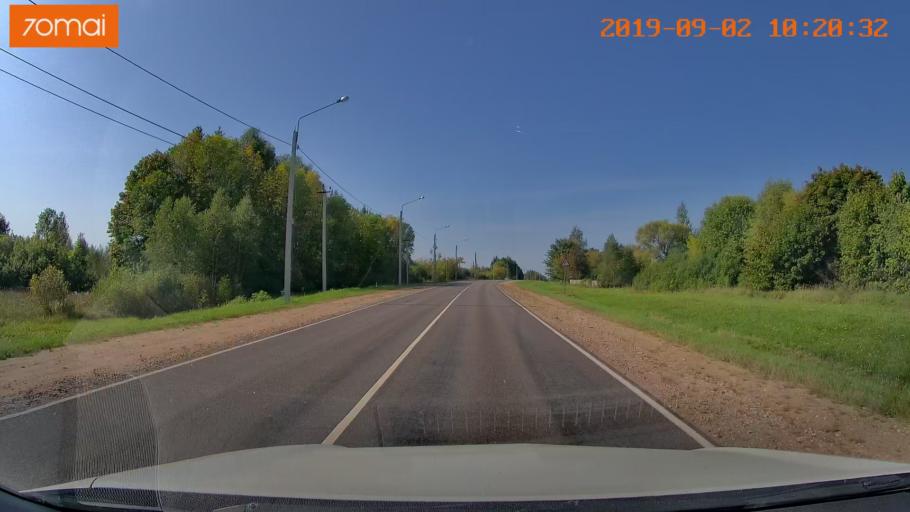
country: RU
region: Kaluga
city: Spas-Demensk
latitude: 54.3851
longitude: 34.1726
